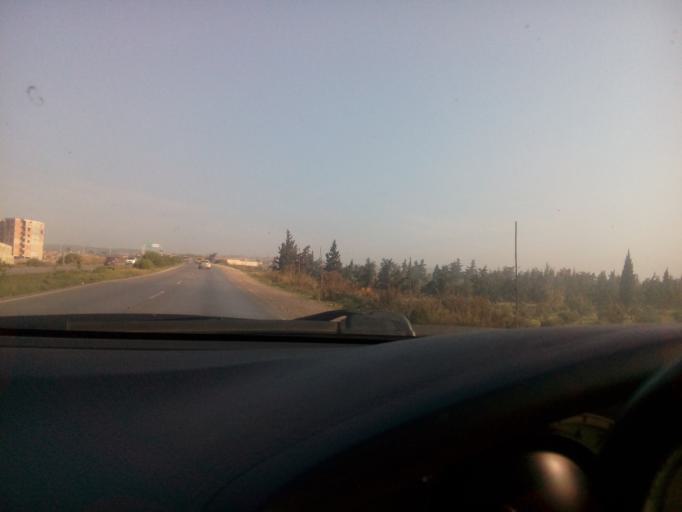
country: DZ
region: Oran
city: Es Senia
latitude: 35.6204
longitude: -0.7185
